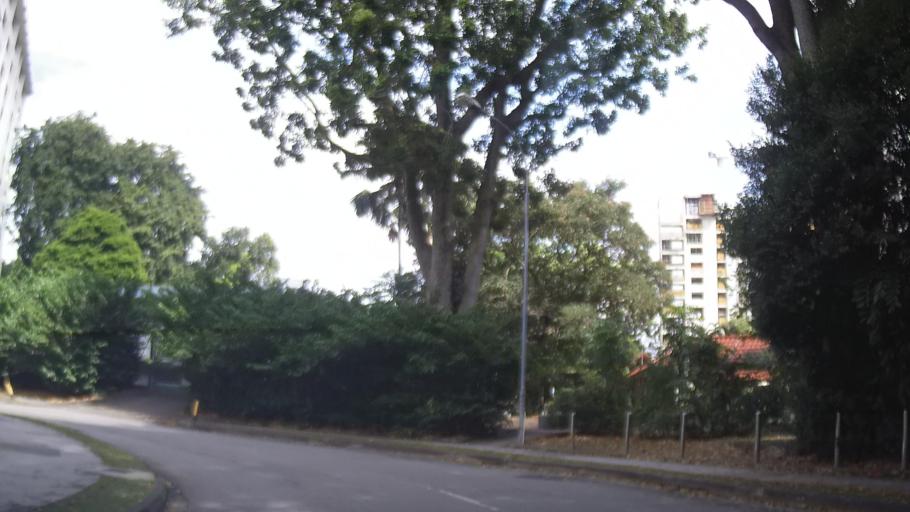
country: SG
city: Singapore
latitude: 1.3186
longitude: 103.8779
